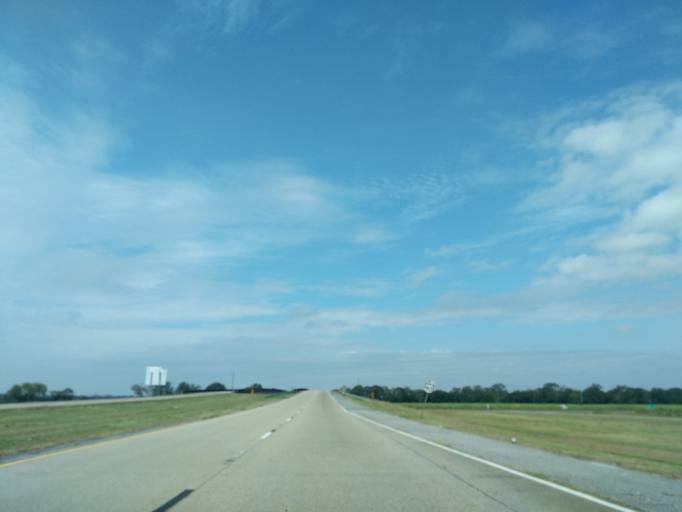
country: US
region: Louisiana
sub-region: Saint Mary Parish
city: Franklin
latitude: 29.7585
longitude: -91.4614
